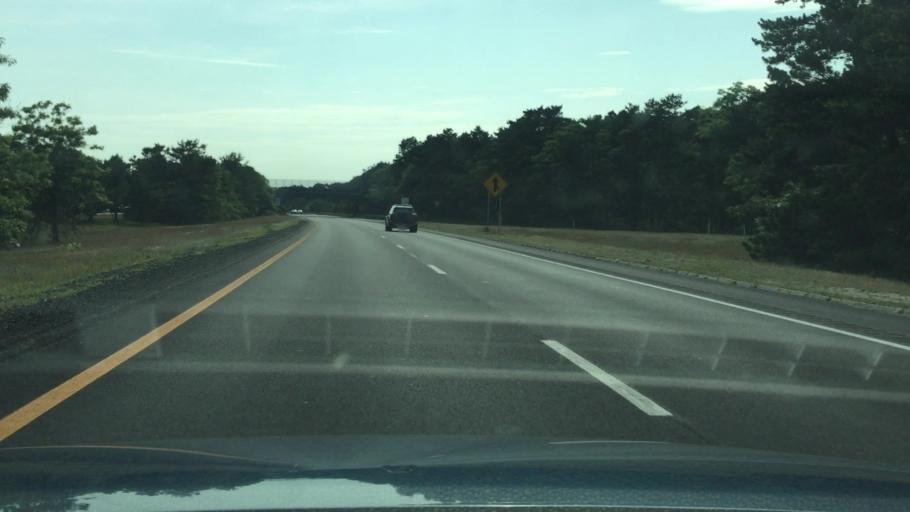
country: US
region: Massachusetts
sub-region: Barnstable County
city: South Dennis
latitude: 41.6989
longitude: -70.1513
